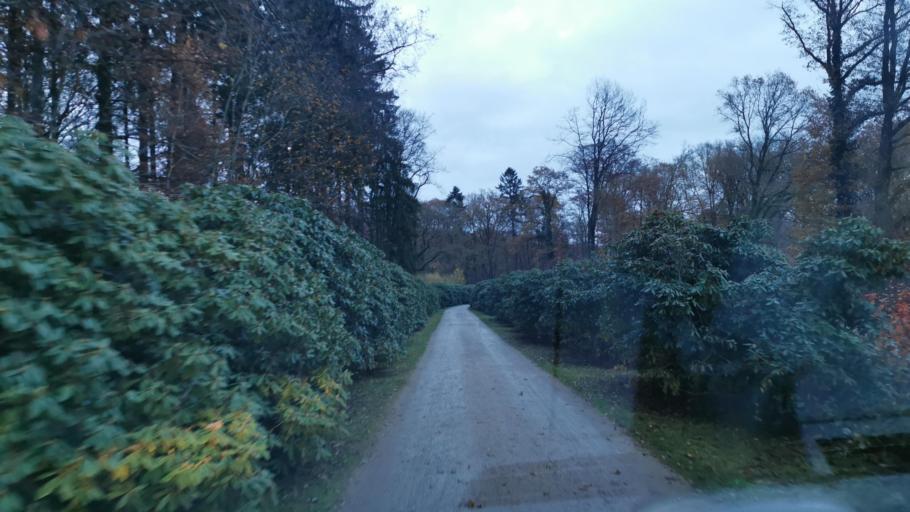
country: NL
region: Overijssel
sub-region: Gemeente Oldenzaal
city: Oldenzaal
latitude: 52.3130
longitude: 6.9521
